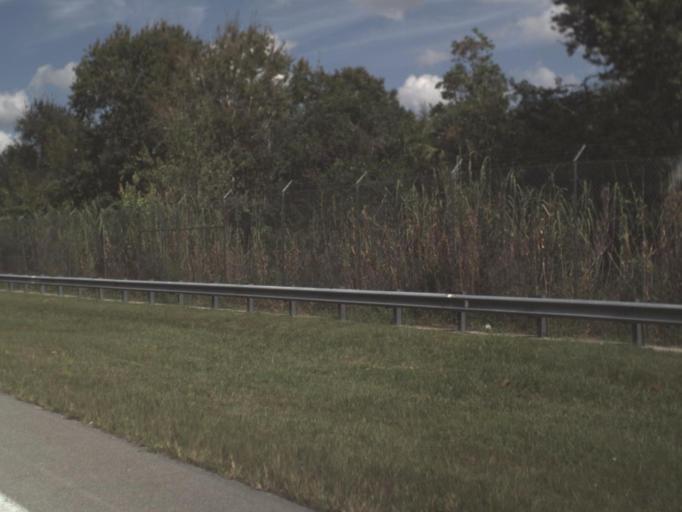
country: US
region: Florida
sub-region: Collier County
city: Orangetree
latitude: 26.0576
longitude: -81.3445
